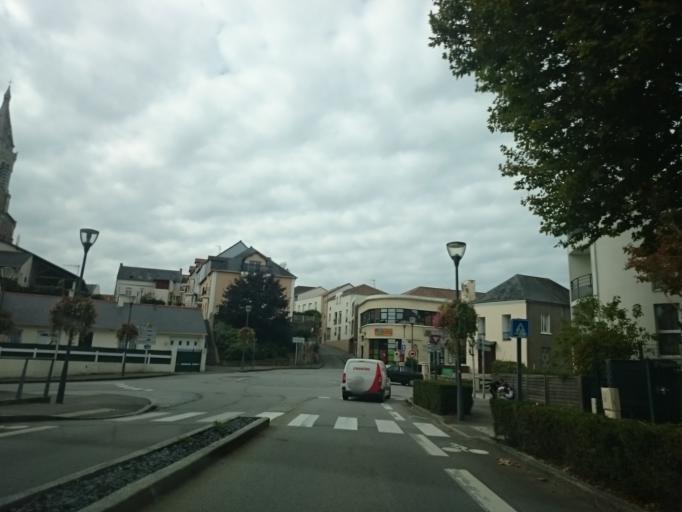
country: FR
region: Pays de la Loire
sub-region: Departement de la Loire-Atlantique
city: Indre
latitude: 47.1996
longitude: -1.6703
